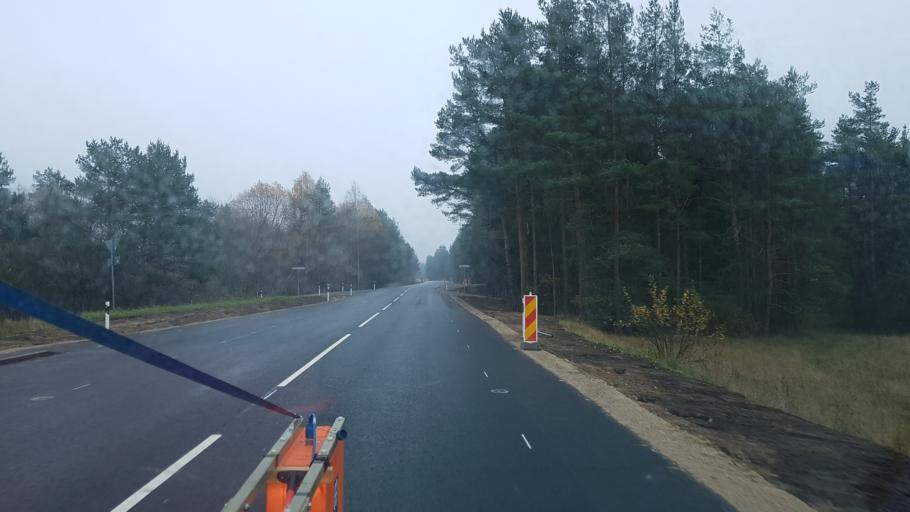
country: EE
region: Raplamaa
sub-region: Kohila vald
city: Kohila
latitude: 59.1806
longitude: 24.7827
